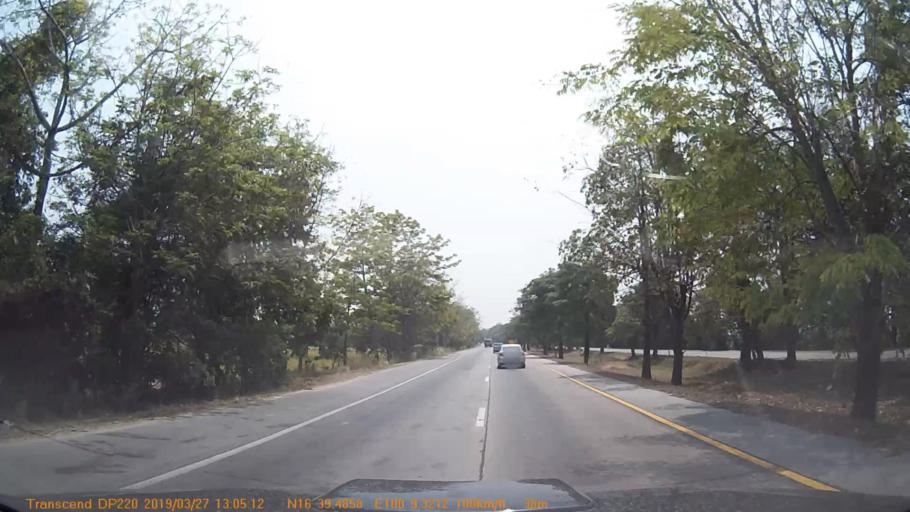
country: TH
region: Phitsanulok
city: Bang Rakam
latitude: 16.6581
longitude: 100.1554
